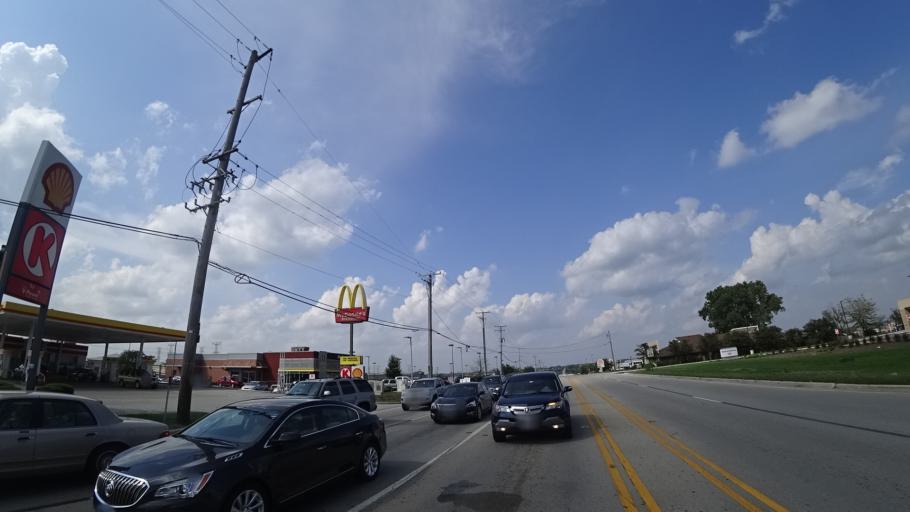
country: US
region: Illinois
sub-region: Will County
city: Goodings Grove
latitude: 41.6293
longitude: -87.9311
